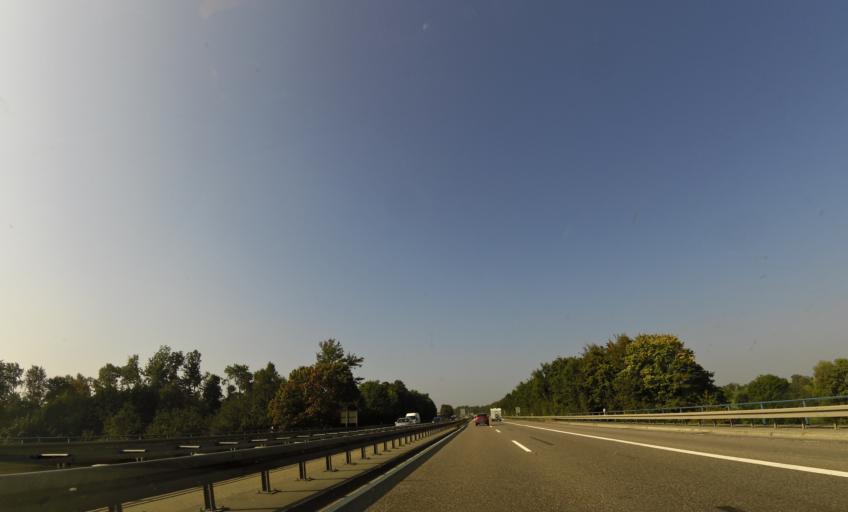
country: DE
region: Baden-Wuerttemberg
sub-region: Regierungsbezirk Stuttgart
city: Bretzfeld
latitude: 49.1955
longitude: 9.4364
